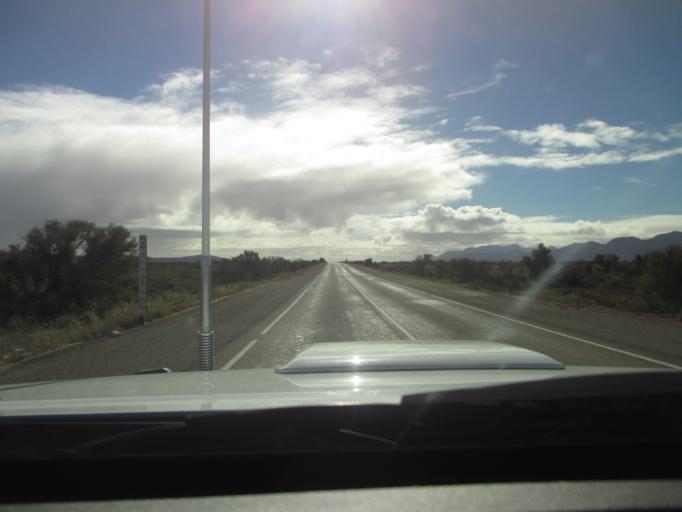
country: AU
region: South Australia
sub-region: Flinders Ranges
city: Quorn
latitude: -31.6992
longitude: 138.3576
